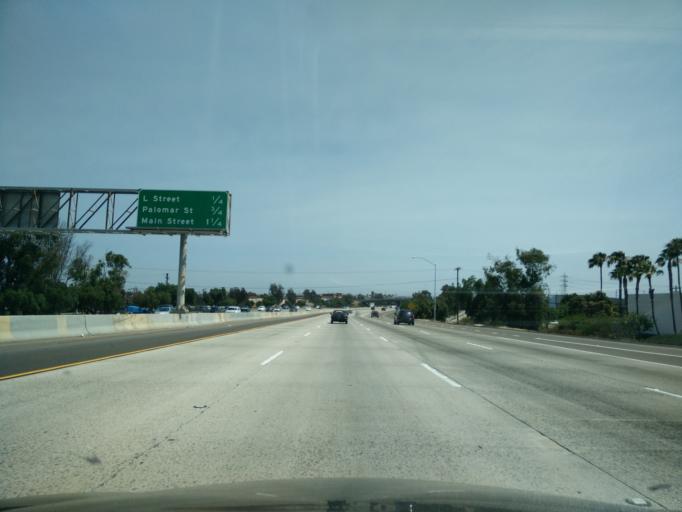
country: US
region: California
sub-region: San Diego County
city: Chula Vista
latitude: 32.6202
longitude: -117.0925
